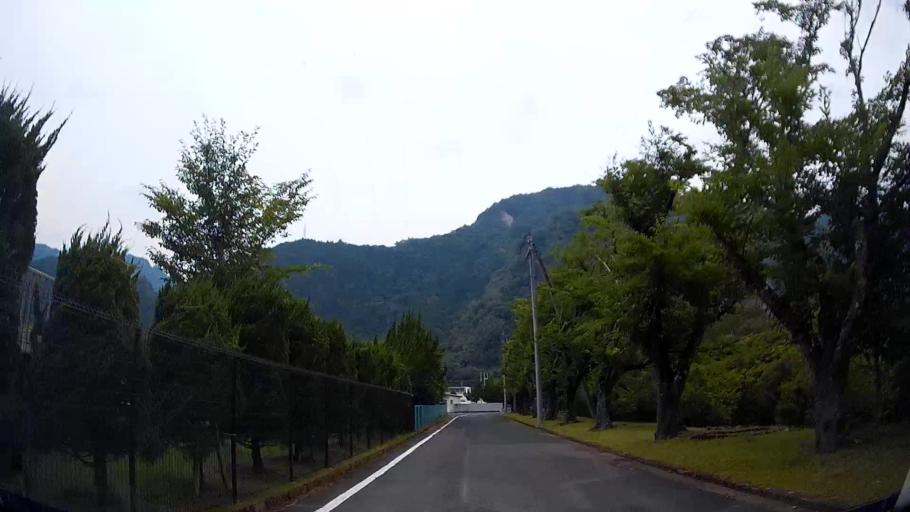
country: JP
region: Shizuoka
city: Mori
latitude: 35.0874
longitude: 137.8072
